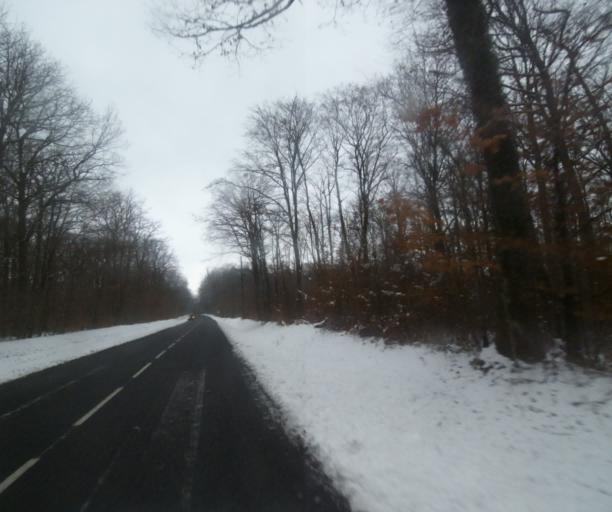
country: FR
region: Champagne-Ardenne
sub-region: Departement de la Haute-Marne
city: Laneuville-a-Remy
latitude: 48.4461
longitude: 4.8626
